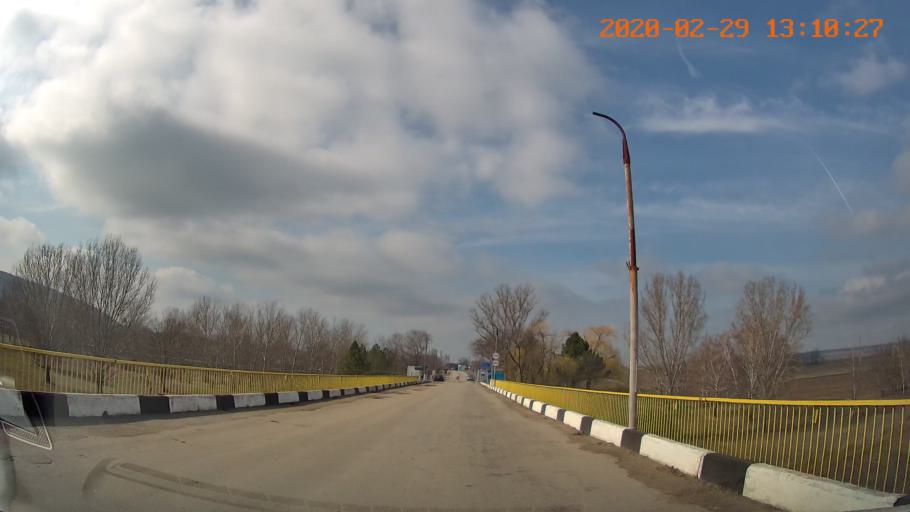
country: MD
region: Telenesti
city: Camenca
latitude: 48.0122
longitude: 28.7004
